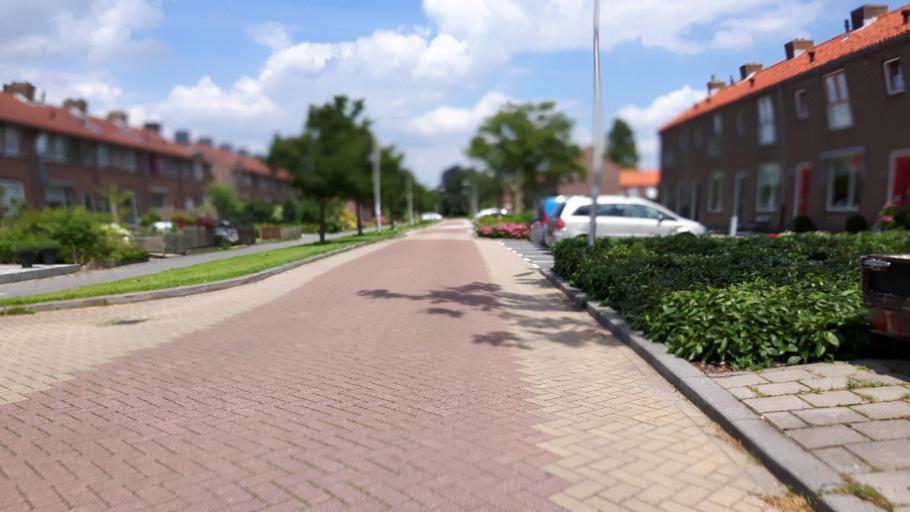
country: NL
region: South Holland
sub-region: Gemeente Boskoop
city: Boskoop
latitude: 52.0787
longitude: 4.6796
